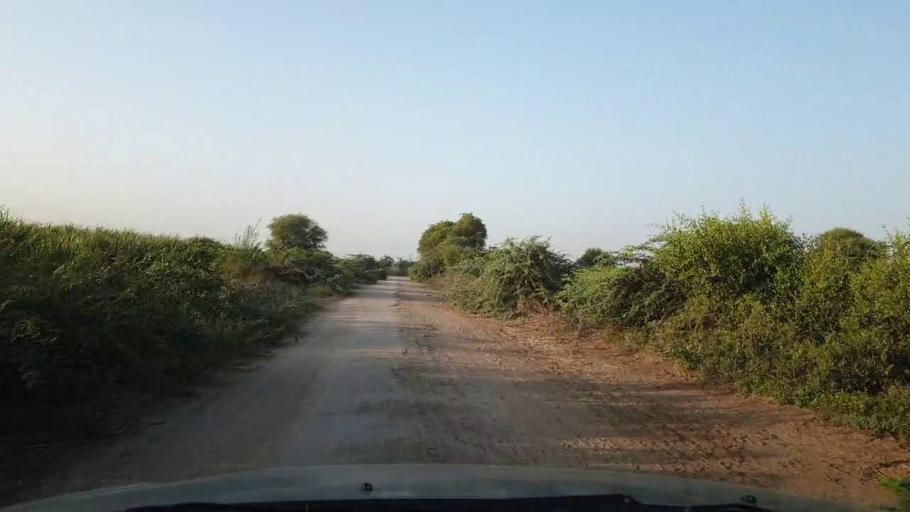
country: PK
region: Sindh
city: Tando Ghulam Ali
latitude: 25.1094
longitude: 68.9486
